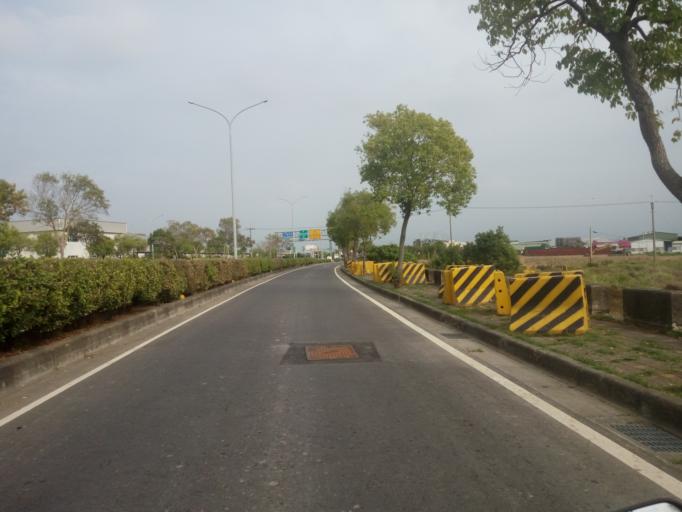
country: TW
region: Taiwan
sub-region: Chiayi
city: Jiayi Shi
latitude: 23.4893
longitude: 120.3932
